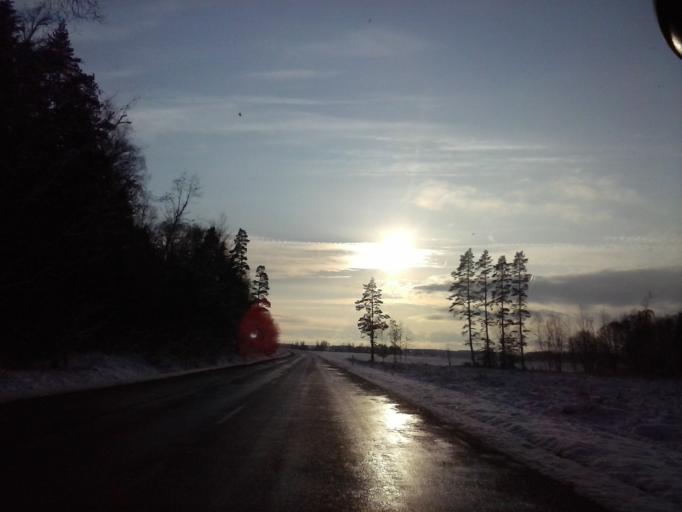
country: EE
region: Tartu
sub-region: UElenurme vald
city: Ulenurme
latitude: 58.3293
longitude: 26.8884
